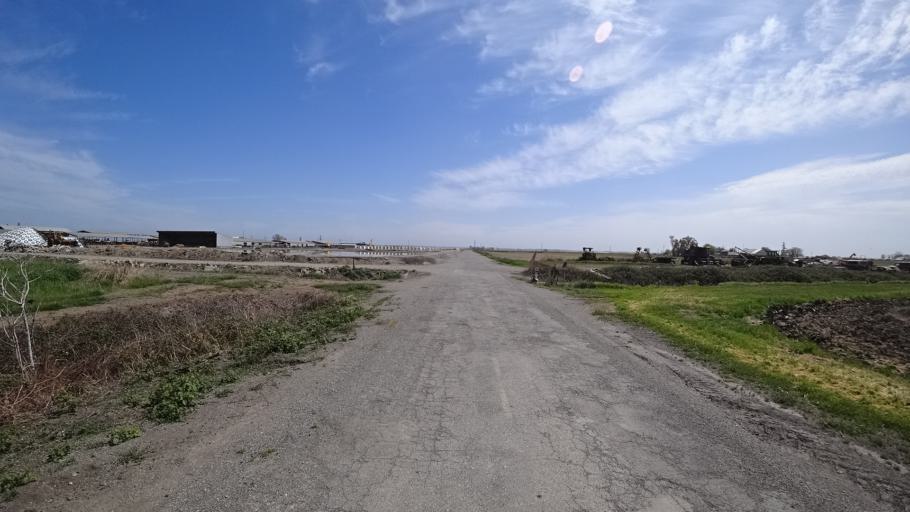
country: US
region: California
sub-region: Glenn County
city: Willows
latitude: 39.5726
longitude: -122.0701
